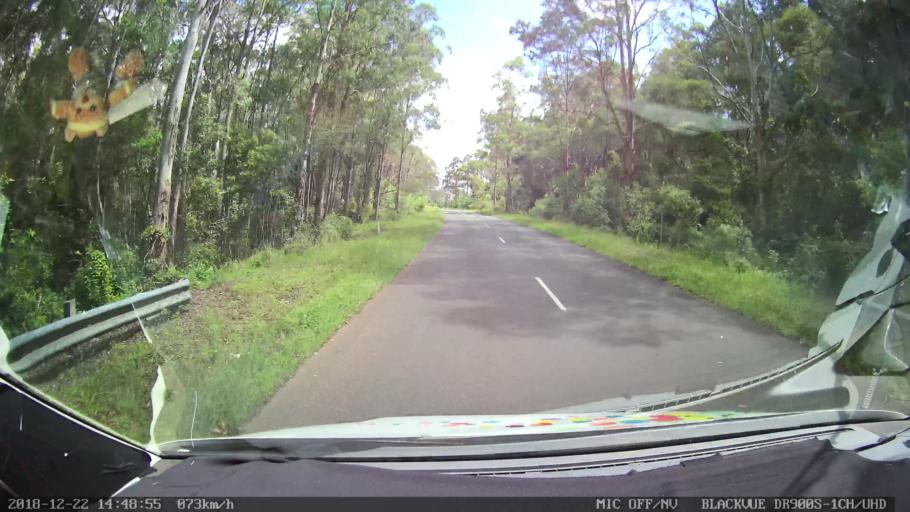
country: AU
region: New South Wales
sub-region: Bellingen
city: Dorrigo
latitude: -30.1851
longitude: 152.5512
